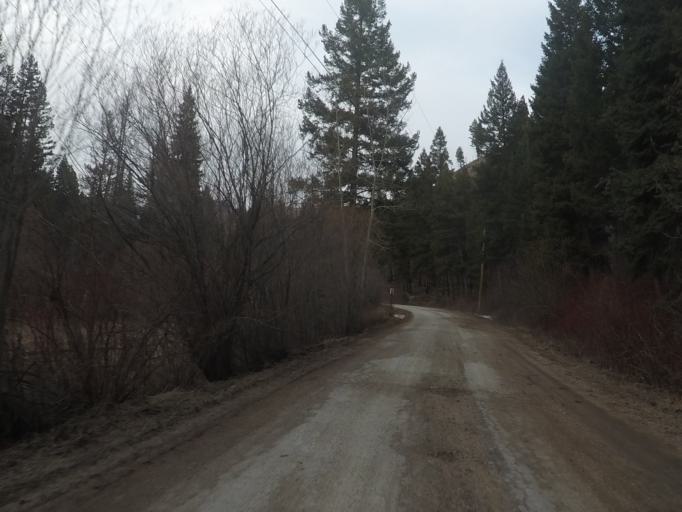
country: US
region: Montana
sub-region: Ravalli County
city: Hamilton
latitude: 45.8468
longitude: -114.0350
